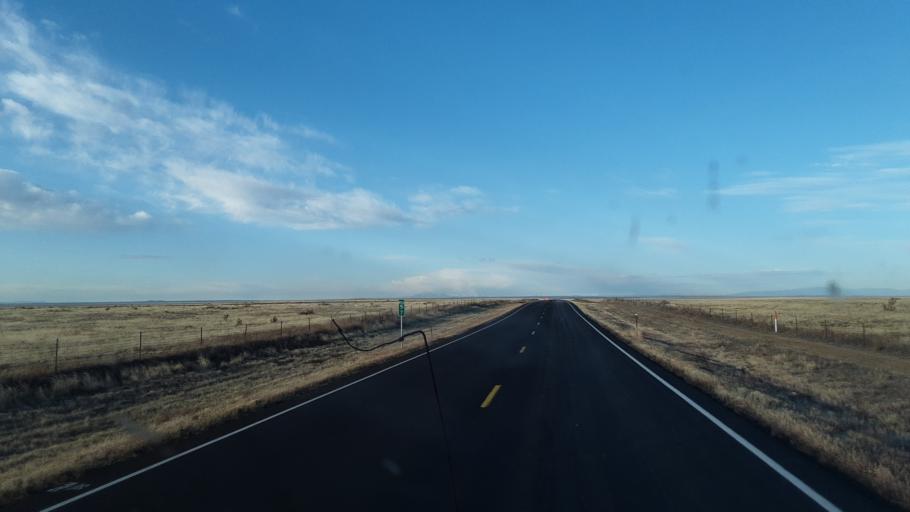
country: US
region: Colorado
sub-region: Otero County
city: Rocky Ford
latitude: 37.9688
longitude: -103.8243
